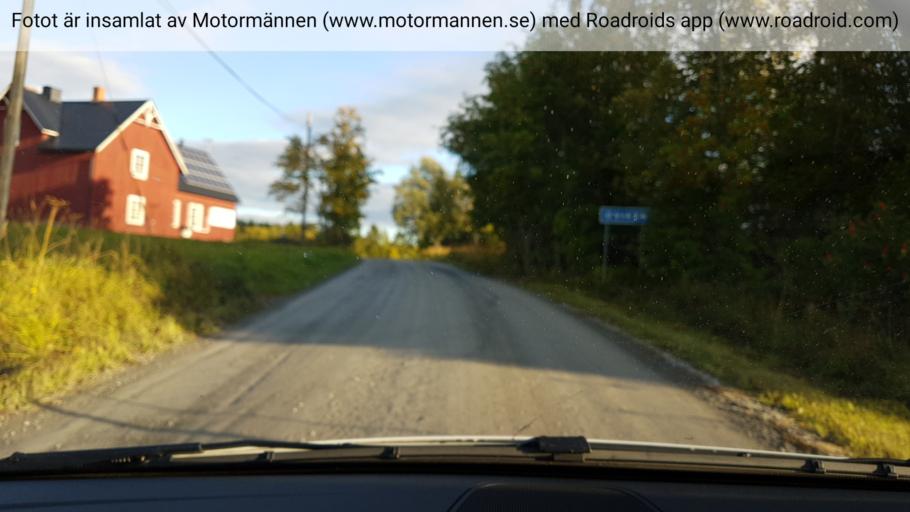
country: SE
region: Jaemtland
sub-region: Bergs Kommun
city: Hoverberg
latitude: 63.0031
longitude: 14.3906
